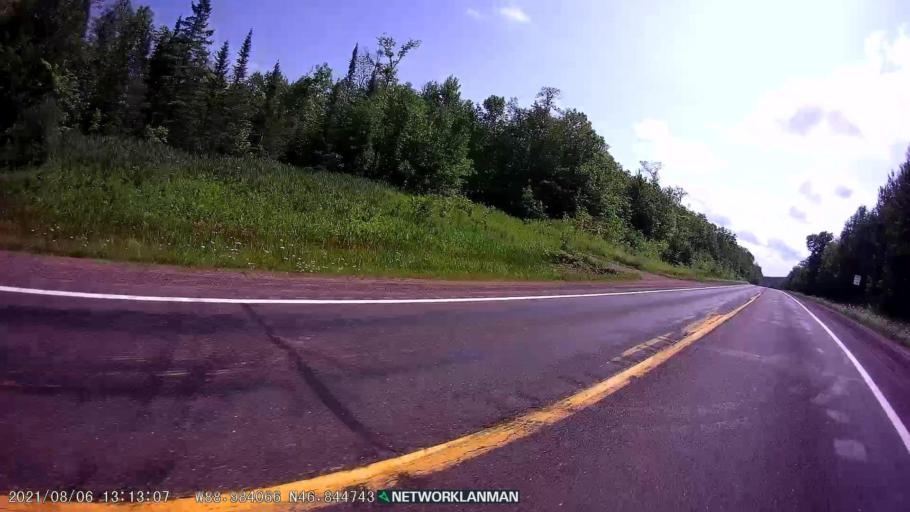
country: US
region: Michigan
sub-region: Ontonagon County
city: Ontonagon
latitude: 46.8443
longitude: -88.9845
